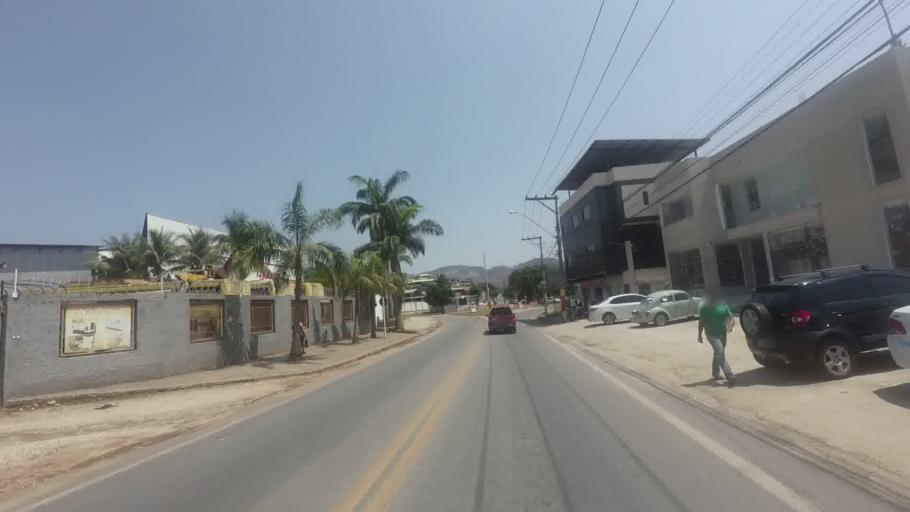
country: BR
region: Espirito Santo
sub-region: Cachoeiro De Itapemirim
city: Cachoeiro de Itapemirim
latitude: -20.8327
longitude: -41.1767
